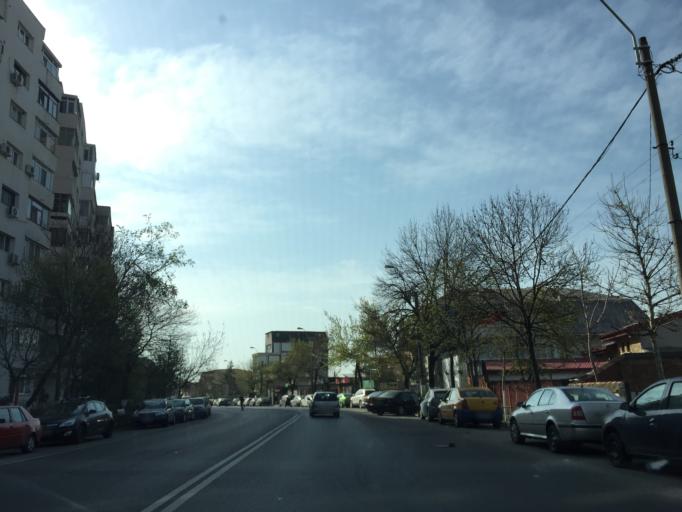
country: RO
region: Bucuresti
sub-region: Municipiul Bucuresti
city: Bucharest
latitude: 44.4137
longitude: 26.1334
